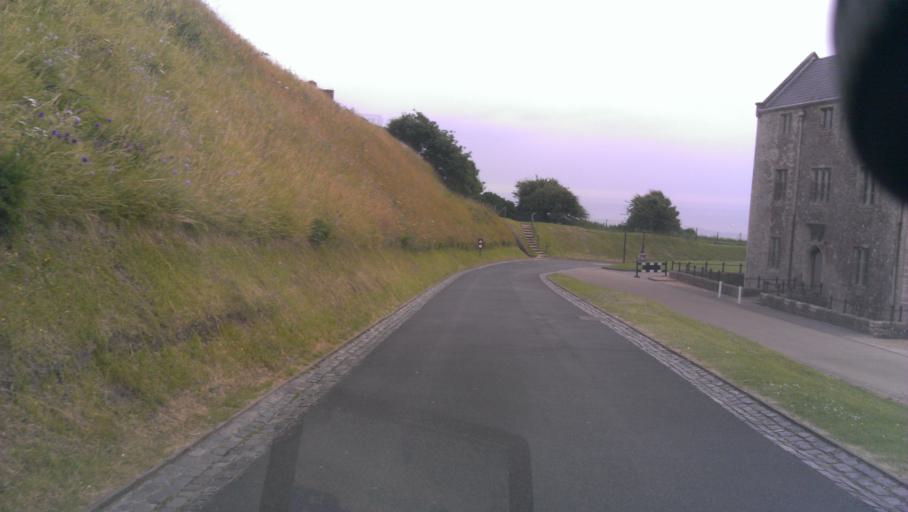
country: GB
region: England
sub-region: Kent
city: Dover
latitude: 51.1281
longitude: 1.3253
